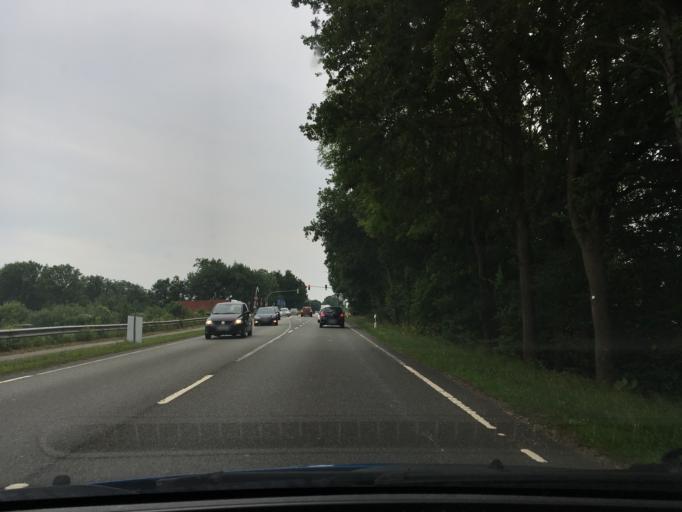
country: DE
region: Lower Saxony
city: Wenzendorf
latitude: 53.3736
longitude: 9.8042
